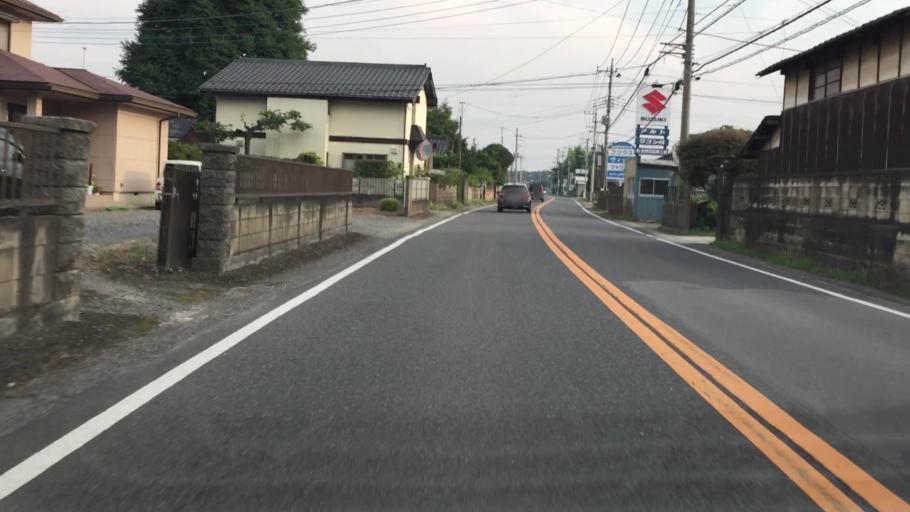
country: JP
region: Tochigi
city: Fujioka
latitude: 36.3086
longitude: 139.6721
